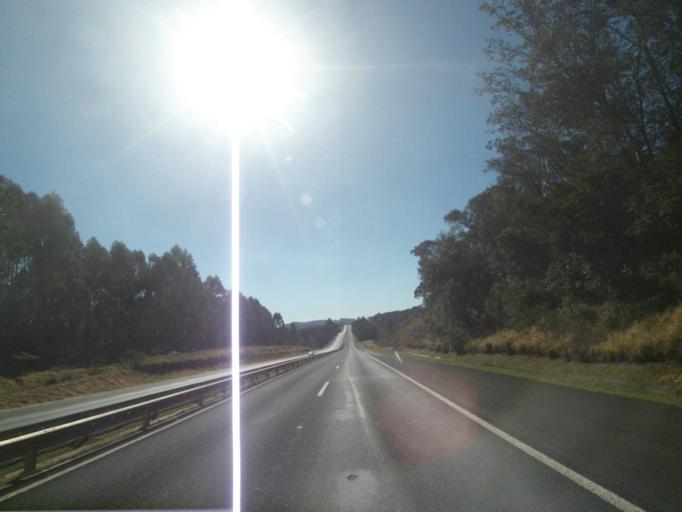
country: BR
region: Parana
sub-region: Tibagi
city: Tibagi
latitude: -24.8419
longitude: -50.4752
